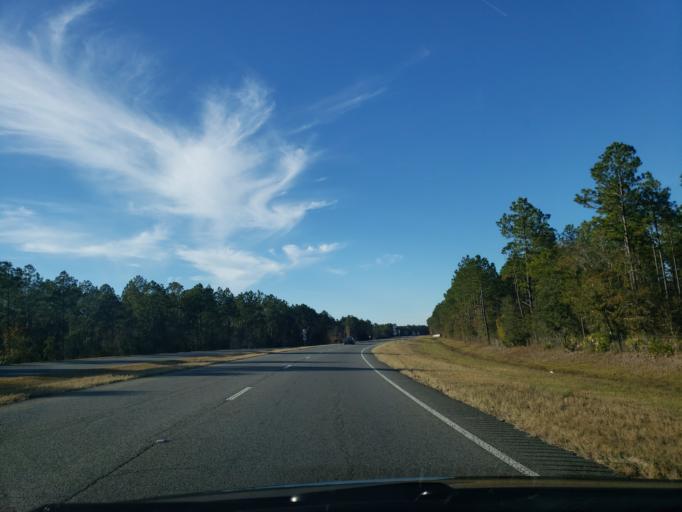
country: US
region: Georgia
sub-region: Ware County
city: Deenwood
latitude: 31.2102
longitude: -82.4149
